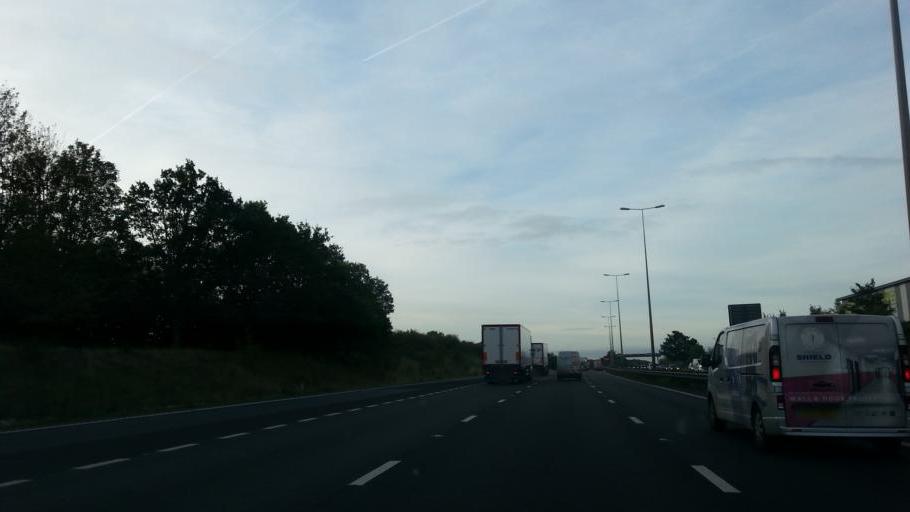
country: GB
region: England
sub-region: Leicestershire
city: Enderby
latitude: 52.5961
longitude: -1.1947
